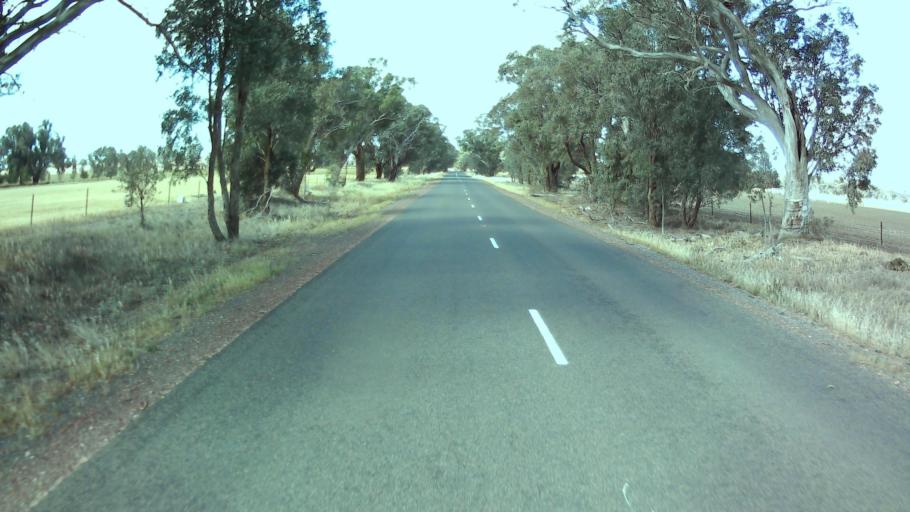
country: AU
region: New South Wales
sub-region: Weddin
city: Grenfell
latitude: -33.9813
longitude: 148.4182
